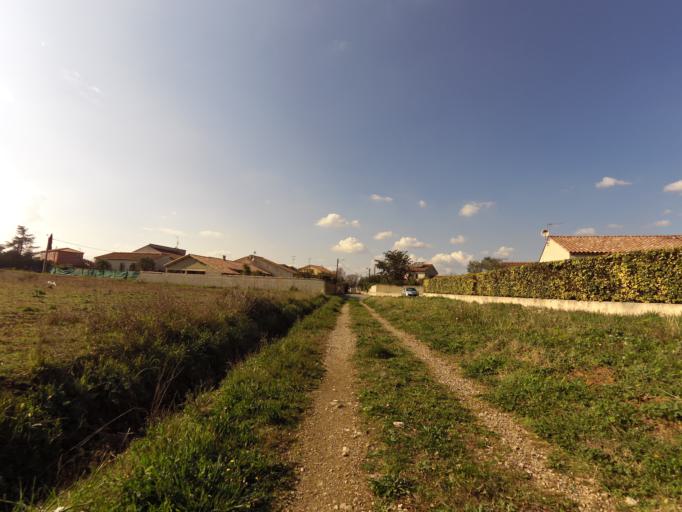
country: FR
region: Languedoc-Roussillon
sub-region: Departement du Gard
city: Codognan
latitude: 43.7253
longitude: 4.2246
